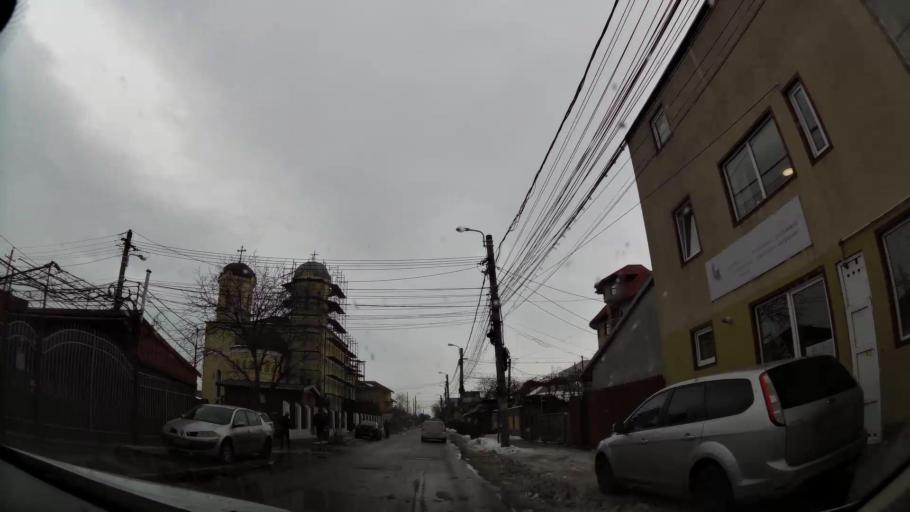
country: RO
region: Ilfov
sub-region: Comuna Pantelimon
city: Pantelimon
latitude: 44.4339
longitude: 26.1985
